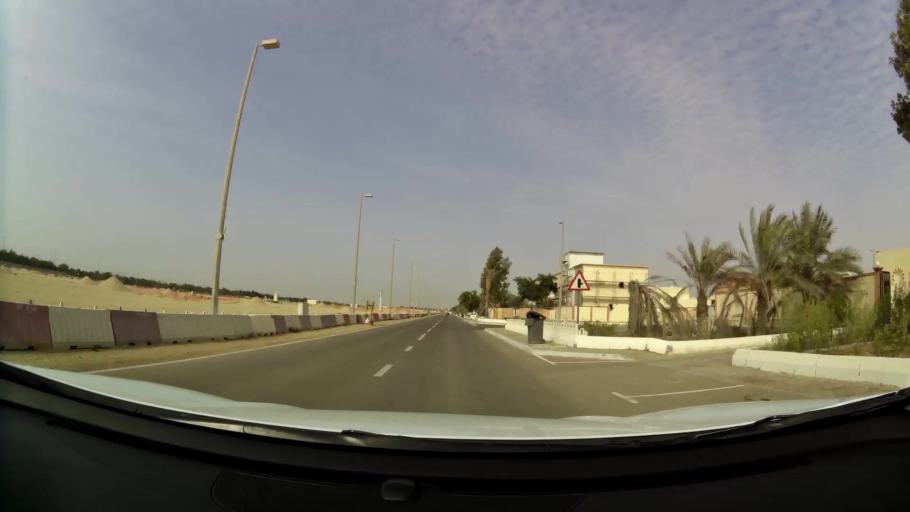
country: AE
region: Abu Dhabi
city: Abu Dhabi
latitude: 24.6094
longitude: 54.7010
